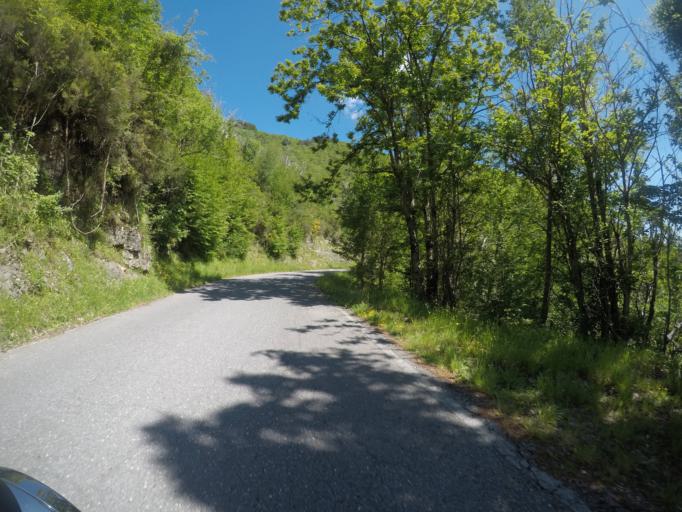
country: IT
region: Tuscany
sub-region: Provincia di Lucca
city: Careggine
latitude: 44.0734
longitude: 10.3308
